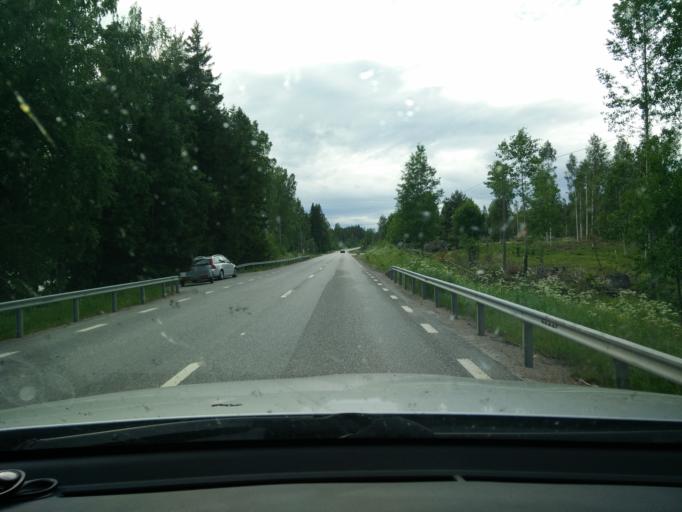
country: SE
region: Gaevleborg
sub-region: Nordanstigs Kommun
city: Bergsjoe
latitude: 62.0869
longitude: 16.7879
